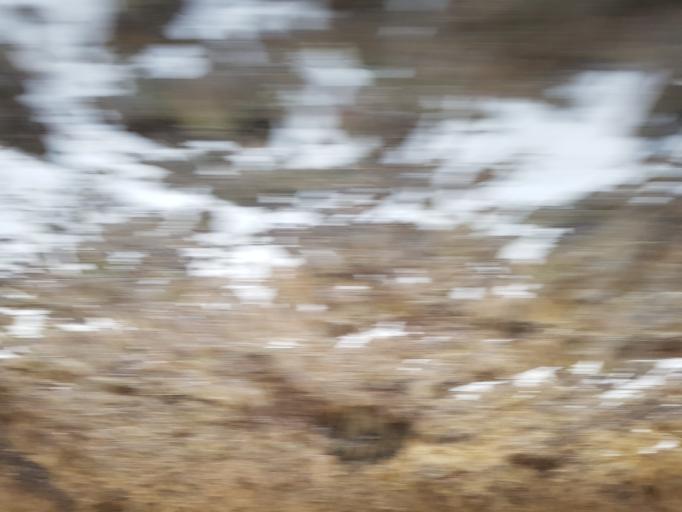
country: NO
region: Sor-Trondelag
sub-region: Midtre Gauldal
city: Storen
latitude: 62.9772
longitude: 10.2264
